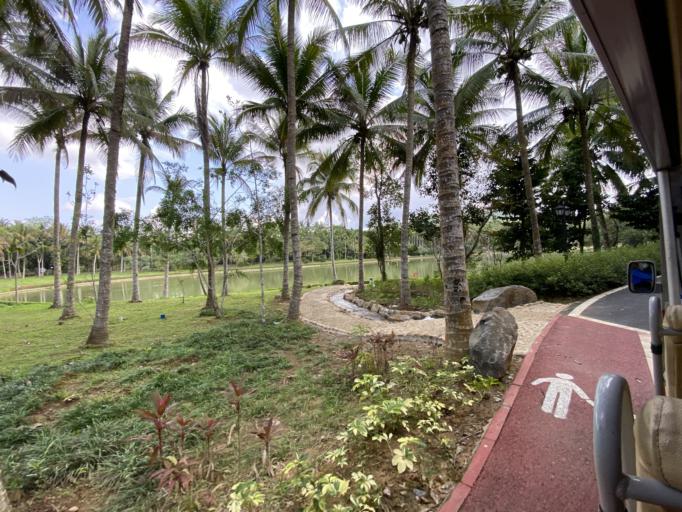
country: CN
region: Hainan
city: Nanqiao
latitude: 18.7345
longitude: 110.1916
